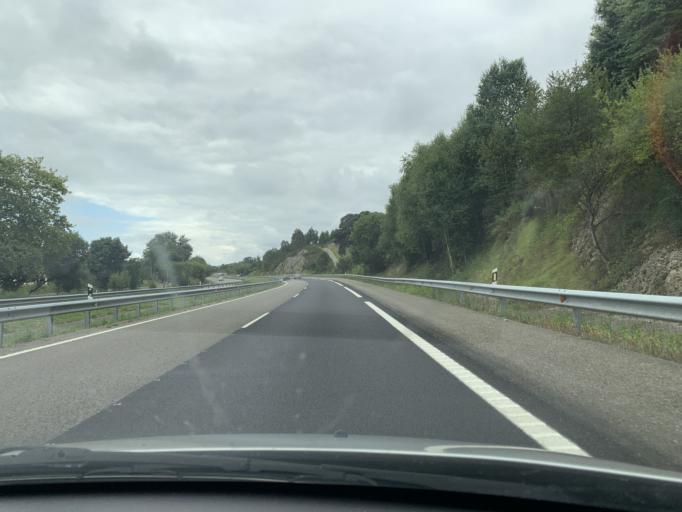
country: ES
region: Asturias
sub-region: Province of Asturias
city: Llanes
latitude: 43.4233
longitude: -4.8062
